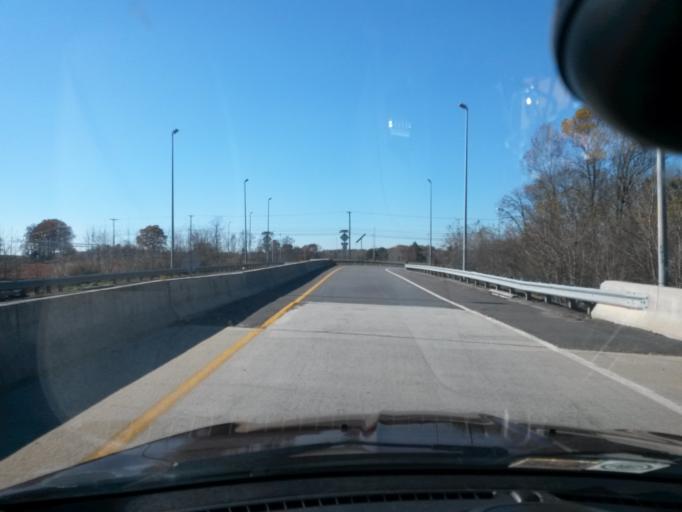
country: US
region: Virginia
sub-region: City of Lynchburg
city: West Lynchburg
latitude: 37.3385
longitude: -79.1891
